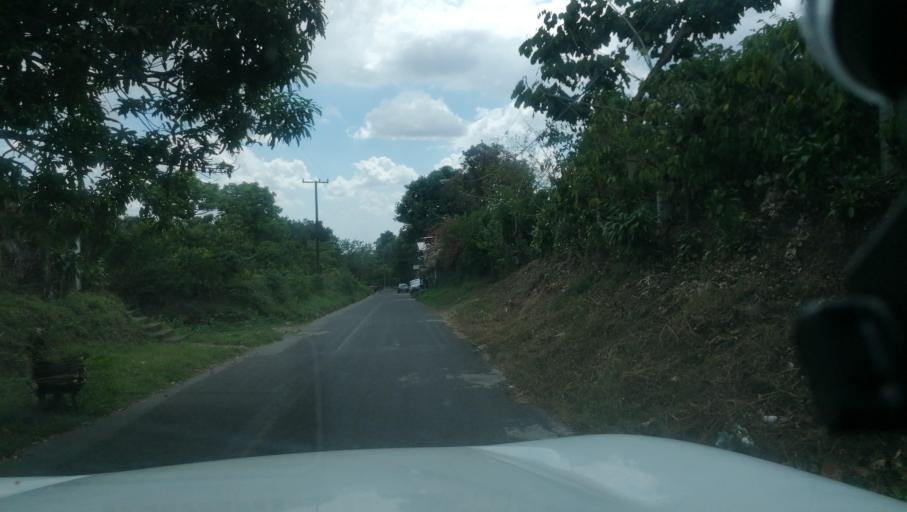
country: MX
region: Chiapas
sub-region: Cacahoatan
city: Benito Juarez
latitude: 15.0382
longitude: -92.1536
